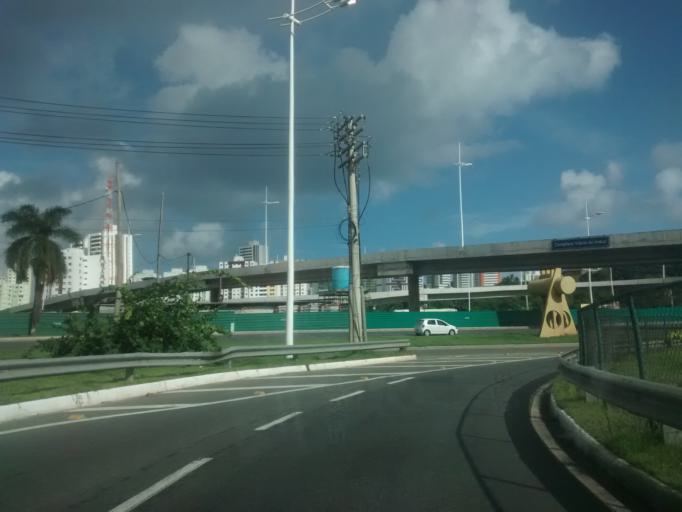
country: BR
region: Bahia
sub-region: Salvador
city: Salvador
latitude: -12.9673
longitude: -38.4402
